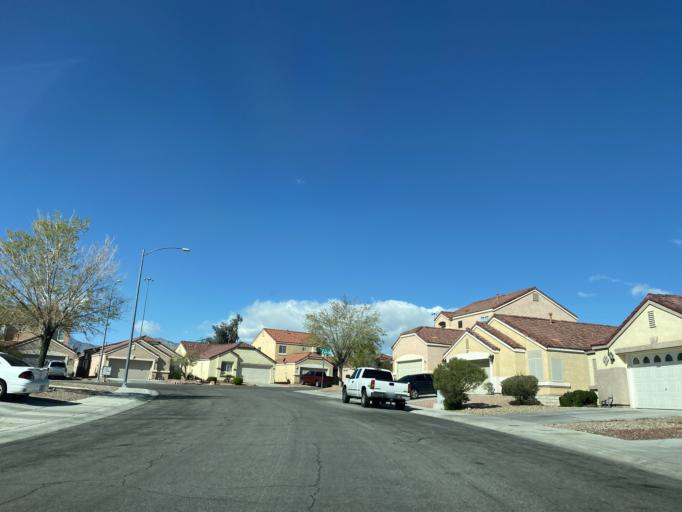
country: US
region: Nevada
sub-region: Clark County
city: Summerlin South
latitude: 36.3054
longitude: -115.2898
